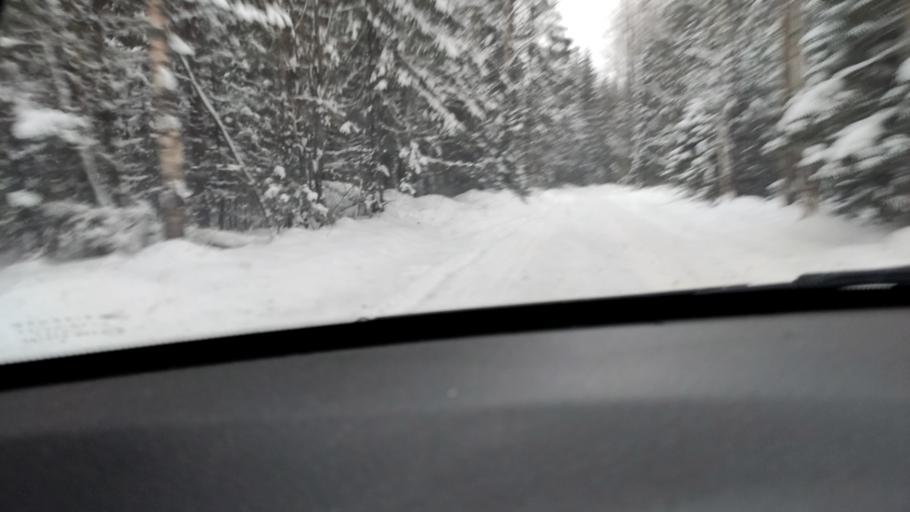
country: RU
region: Perm
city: Krasnokamsk
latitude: 57.9951
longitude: 55.7805
